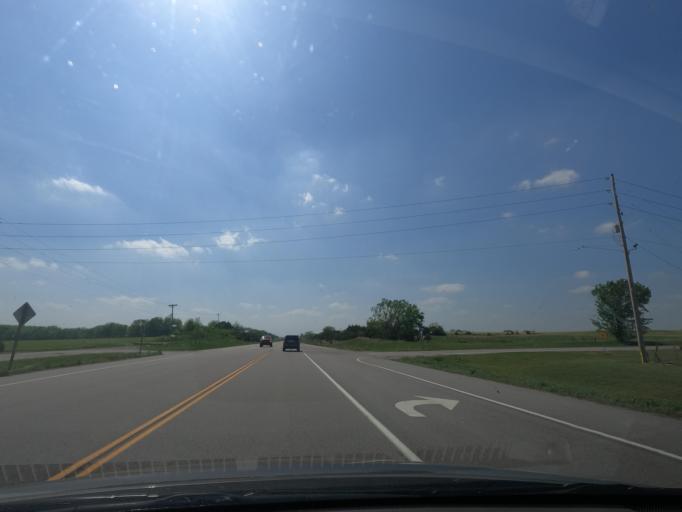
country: US
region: Kansas
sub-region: Butler County
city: El Dorado
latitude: 37.6796
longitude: -96.7887
